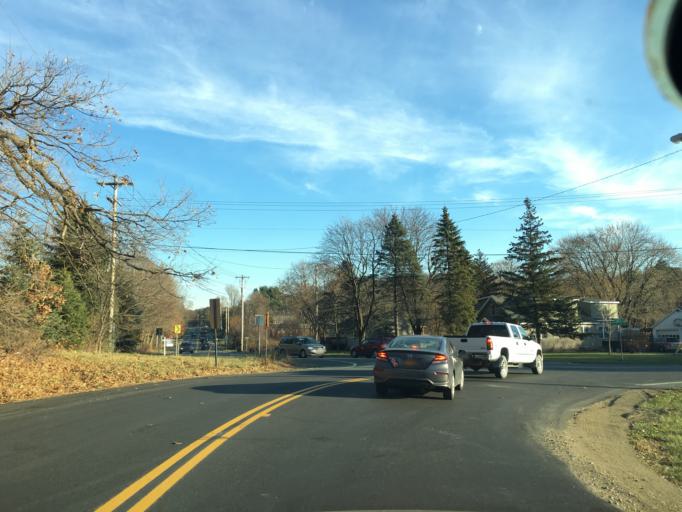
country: US
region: New York
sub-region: Rensselaer County
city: Wynantskill
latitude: 42.6938
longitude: -73.6552
